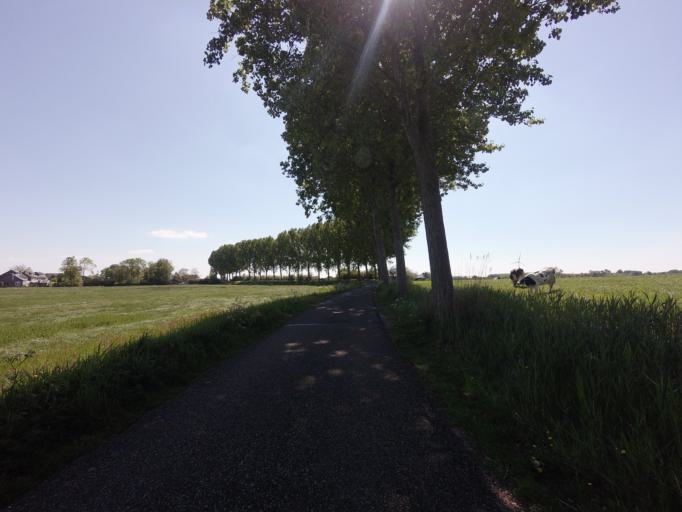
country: NL
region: Utrecht
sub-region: Gemeente De Ronde Venen
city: Mijdrecht
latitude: 52.2223
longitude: 4.8921
